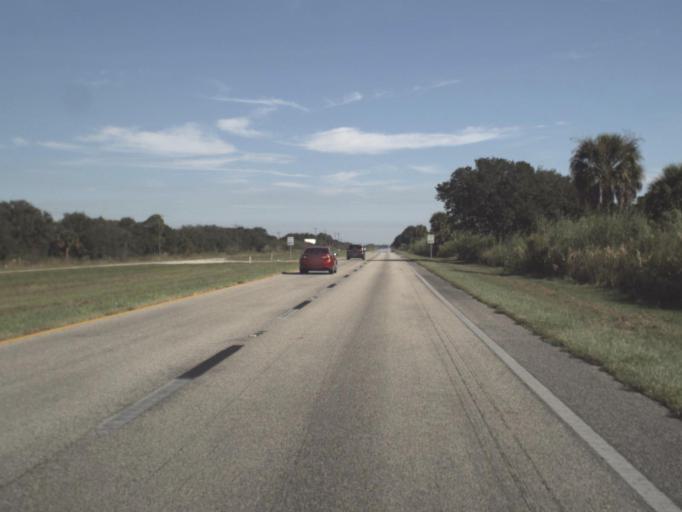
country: US
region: Florida
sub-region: Hendry County
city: Port LaBelle
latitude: 26.9198
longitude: -81.2987
